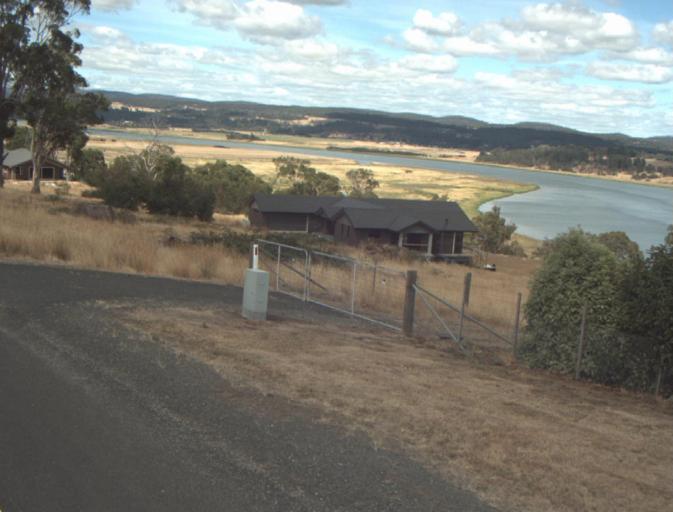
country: AU
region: Tasmania
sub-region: Launceston
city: Mayfield
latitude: -41.3428
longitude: 147.0862
